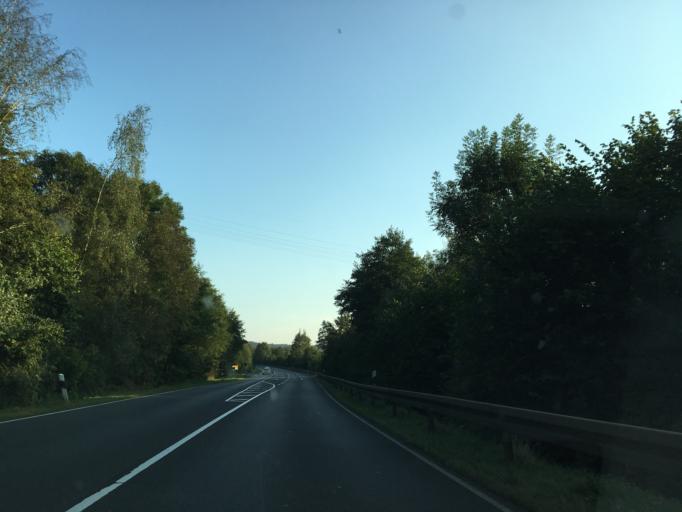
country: DE
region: Hesse
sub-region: Regierungsbezirk Giessen
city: Colbe
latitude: 50.8633
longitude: 8.7921
